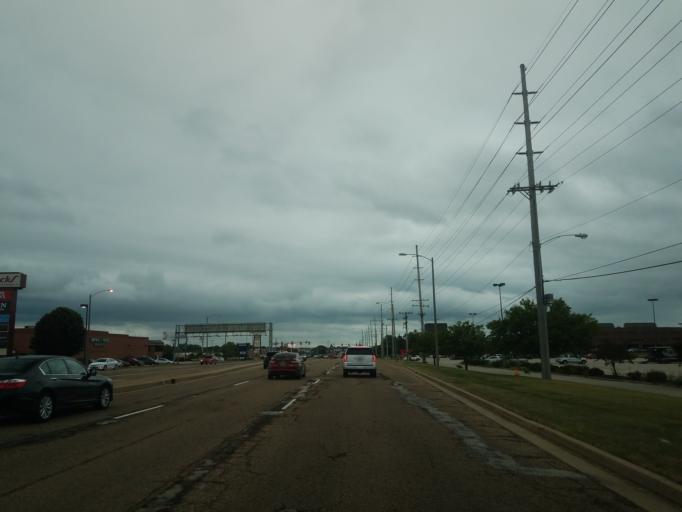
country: US
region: Illinois
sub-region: McLean County
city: Bloomington
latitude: 40.4862
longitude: -88.9530
